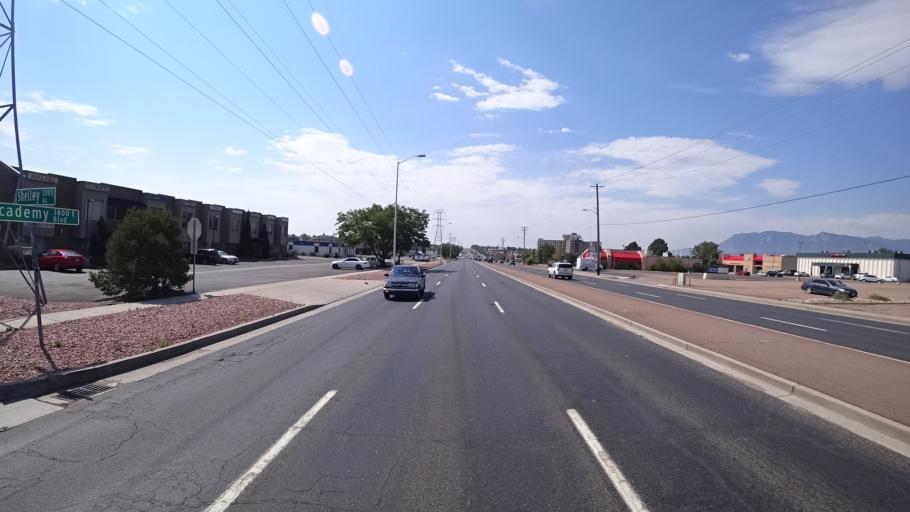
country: US
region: Colorado
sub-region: El Paso County
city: Stratmoor
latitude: 38.8284
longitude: -104.7574
